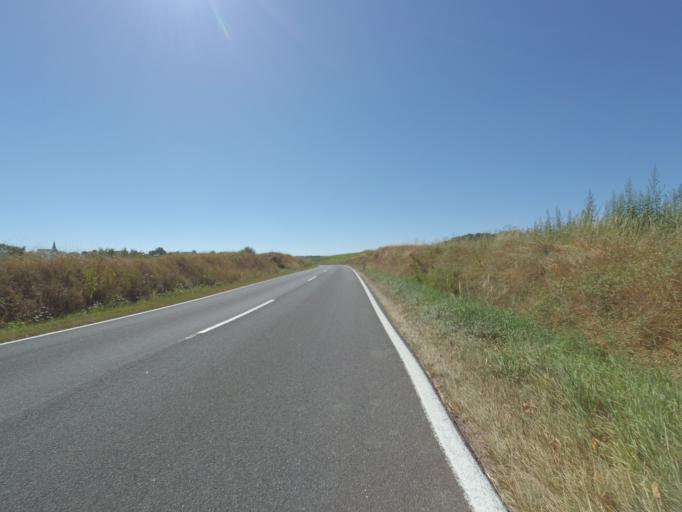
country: DE
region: Rheinland-Pfalz
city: Kliding
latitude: 50.1121
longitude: 7.0520
